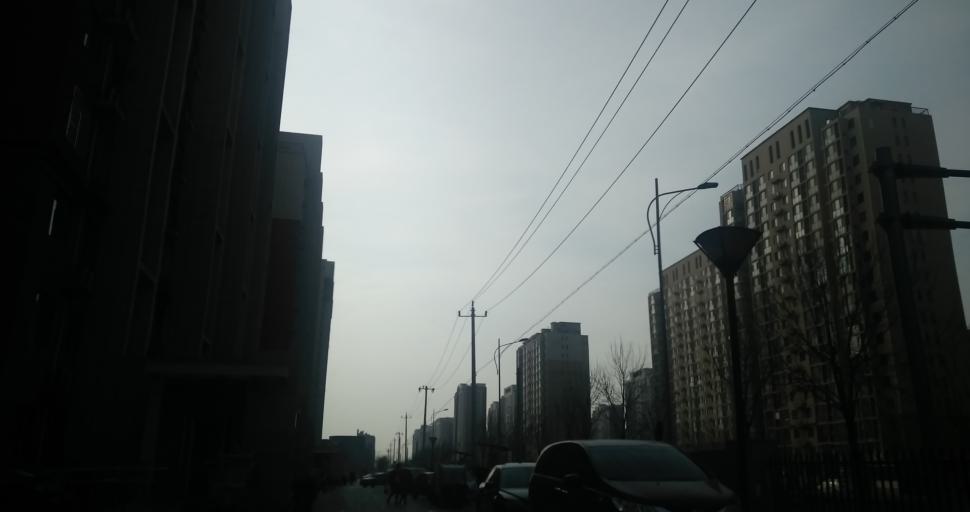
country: CN
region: Beijing
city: Yinghai
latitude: 39.7571
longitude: 116.4896
